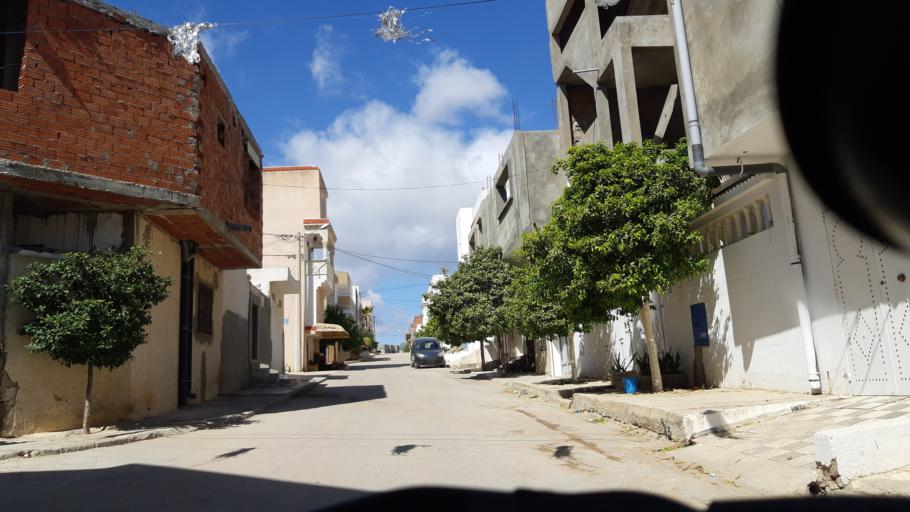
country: TN
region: Susah
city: Akouda
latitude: 35.8928
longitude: 10.5332
